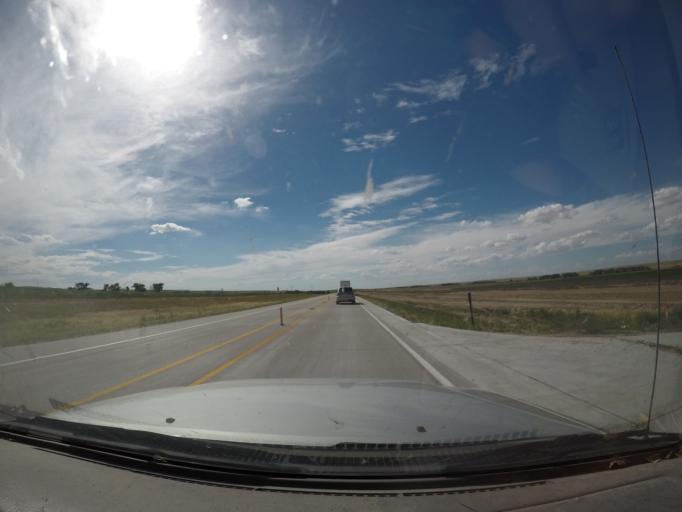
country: US
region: Nebraska
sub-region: Deuel County
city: Chappell
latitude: 41.0974
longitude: -102.5302
